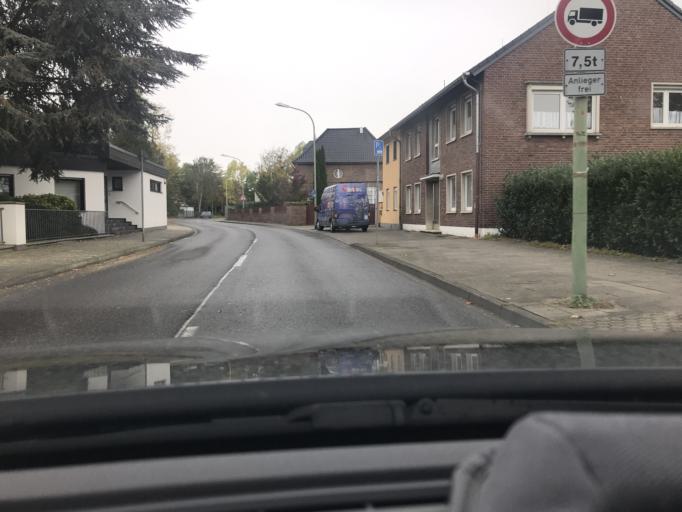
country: DE
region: North Rhine-Westphalia
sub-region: Regierungsbezirk Koln
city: Dueren
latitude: 50.8230
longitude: 6.4595
